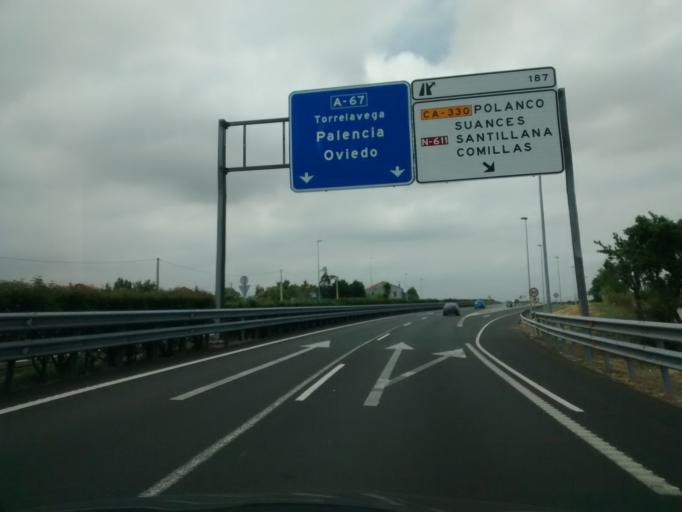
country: ES
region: Cantabria
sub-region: Provincia de Cantabria
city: Polanco
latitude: 43.3918
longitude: -4.0166
